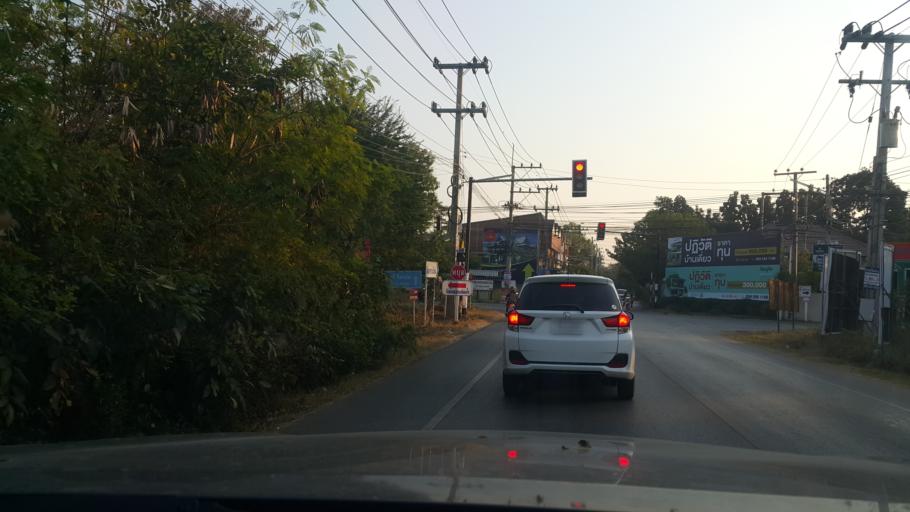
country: TH
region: Nakhon Ratchasima
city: Nakhon Ratchasima
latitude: 14.9385
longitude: 102.0281
